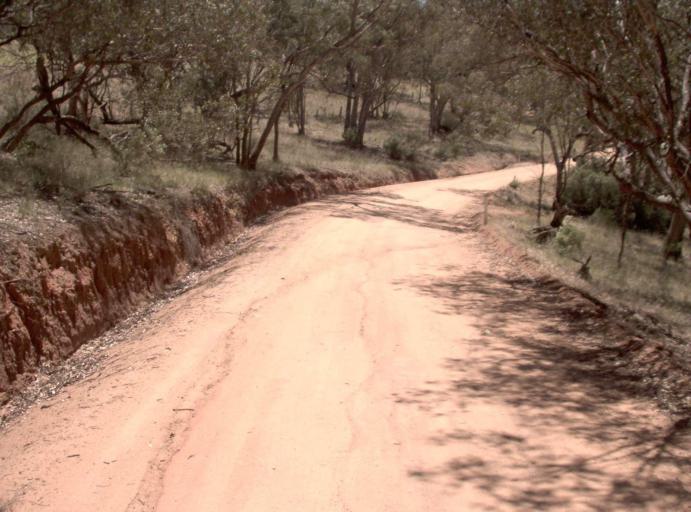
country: AU
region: New South Wales
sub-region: Snowy River
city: Jindabyne
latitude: -36.9632
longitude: 148.3204
